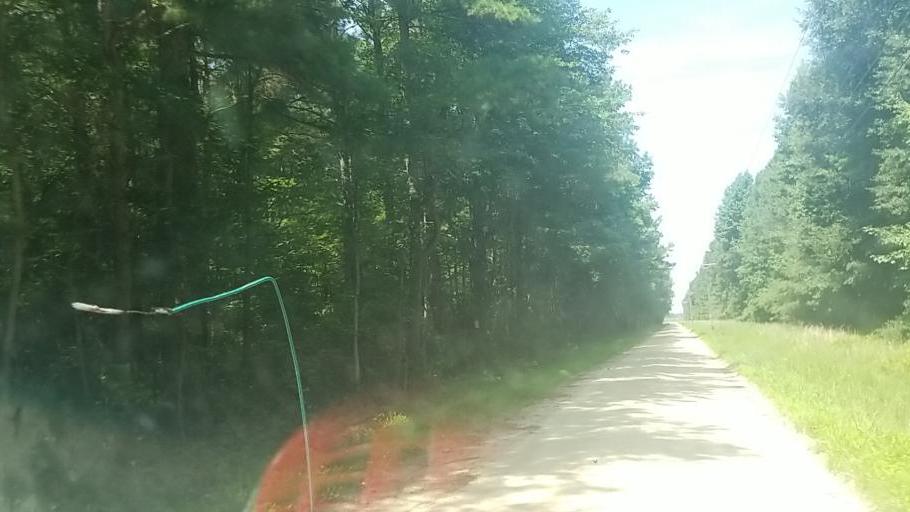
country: US
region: Maryland
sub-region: Caroline County
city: Denton
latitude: 38.8698
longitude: -75.7415
